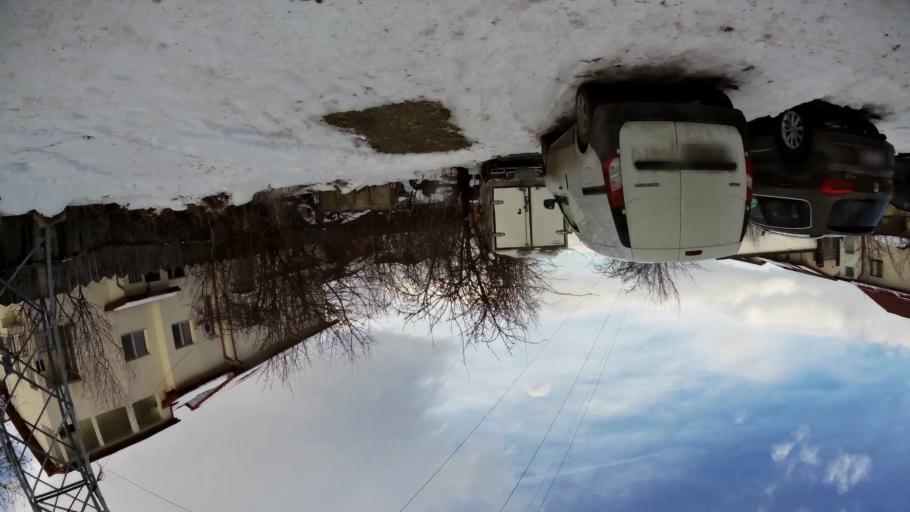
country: RO
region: Ilfov
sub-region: Comuna Fundeni-Dobroesti
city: Fundeni
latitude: 44.4647
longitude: 26.1725
